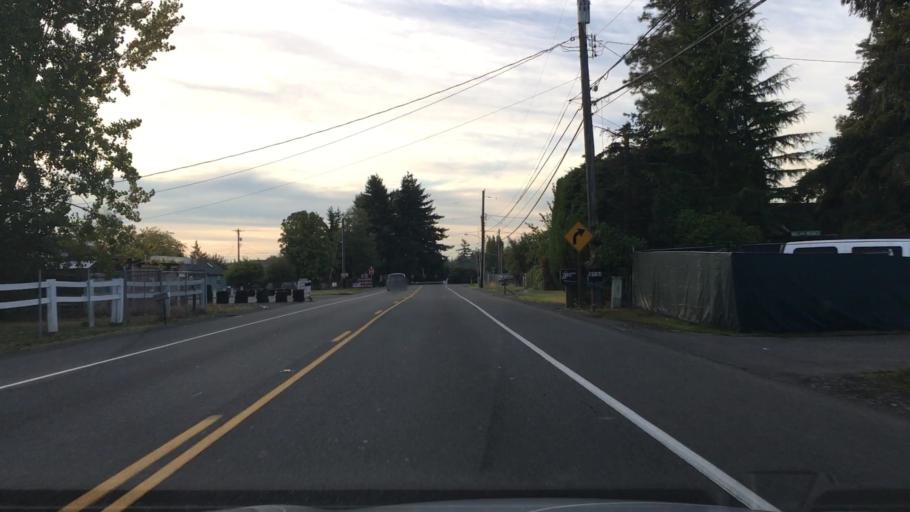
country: US
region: Washington
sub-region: Pierce County
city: Midland
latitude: 47.1738
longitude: -122.4060
